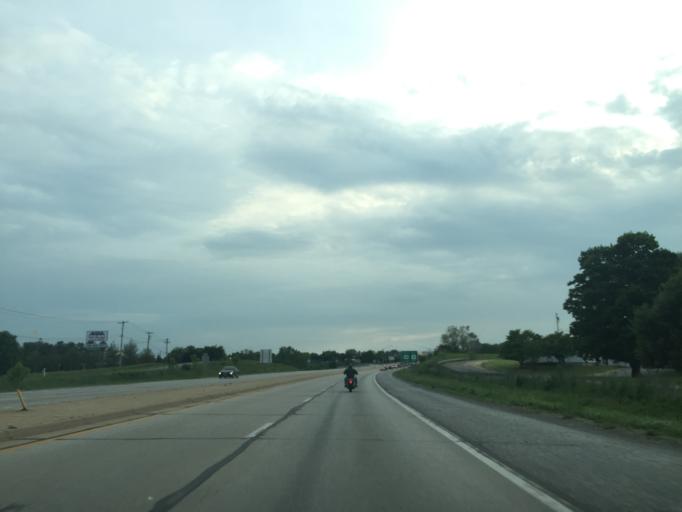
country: US
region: West Virginia
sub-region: Jefferson County
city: Ranson
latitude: 39.2968
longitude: -77.8338
